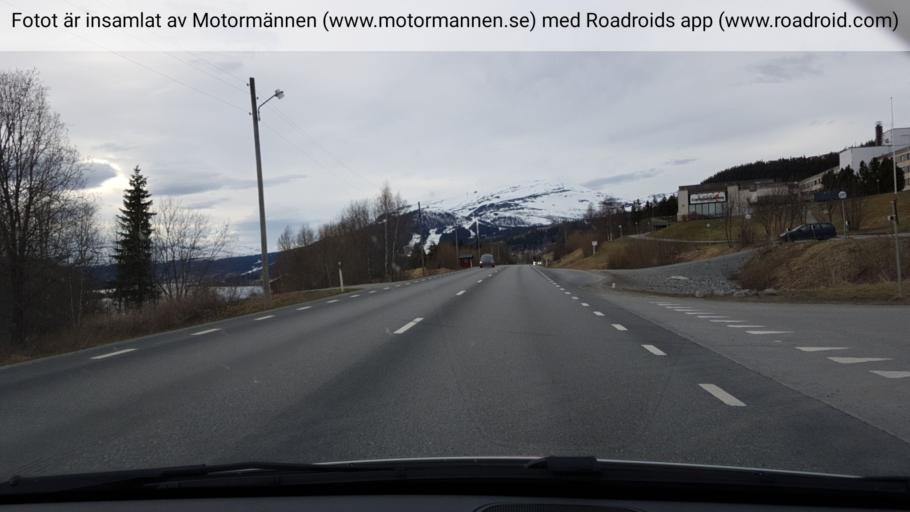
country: SE
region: Jaemtland
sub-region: Are Kommun
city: Are
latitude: 63.3664
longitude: 13.1692
